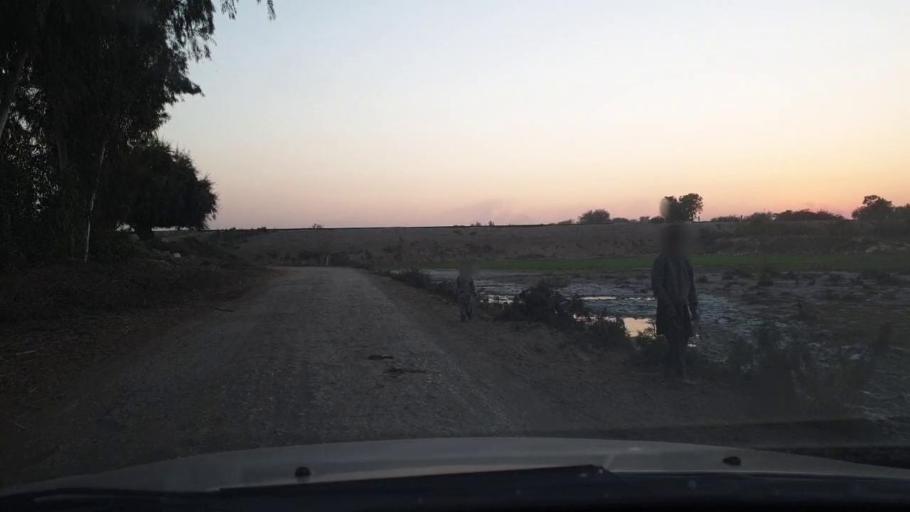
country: PK
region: Sindh
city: Mirpur Mathelo
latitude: 28.0279
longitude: 69.5201
